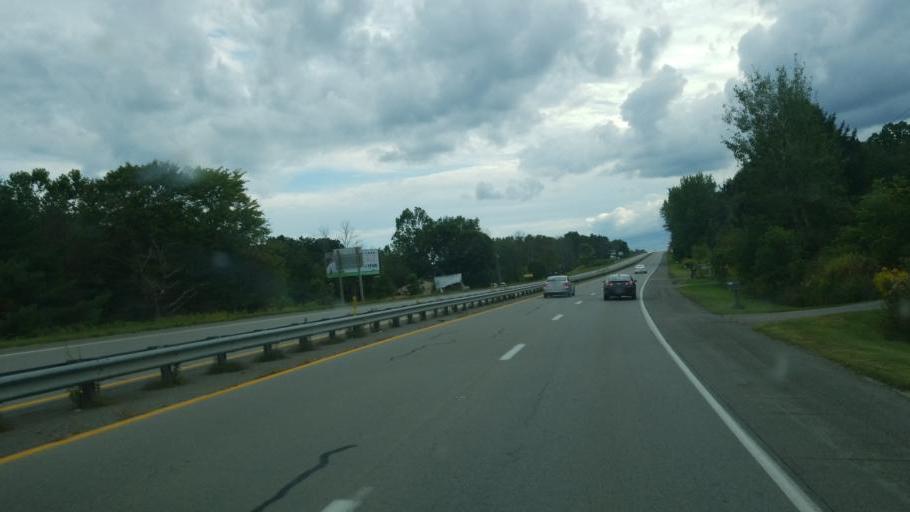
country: US
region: Pennsylvania
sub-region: Mercer County
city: Greenville
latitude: 41.3766
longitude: -80.3986
